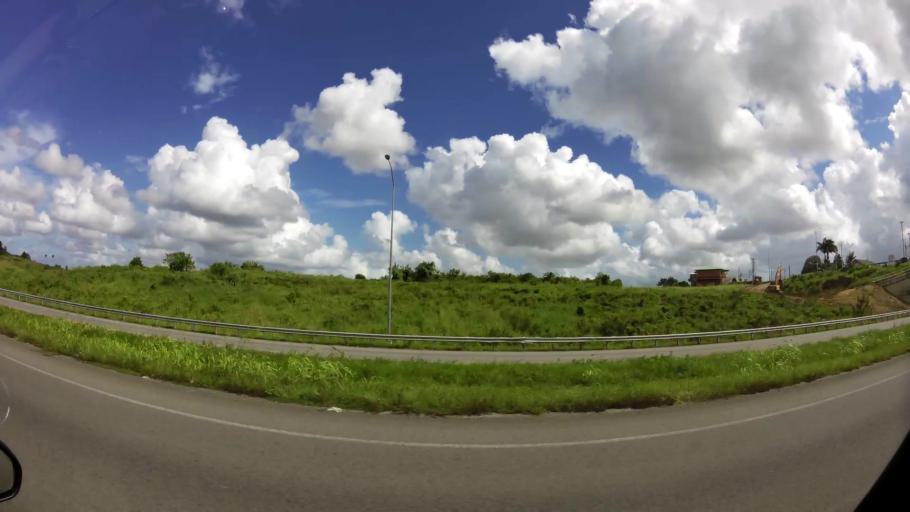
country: TT
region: City of San Fernando
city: Mon Repos
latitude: 10.2466
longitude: -61.4438
